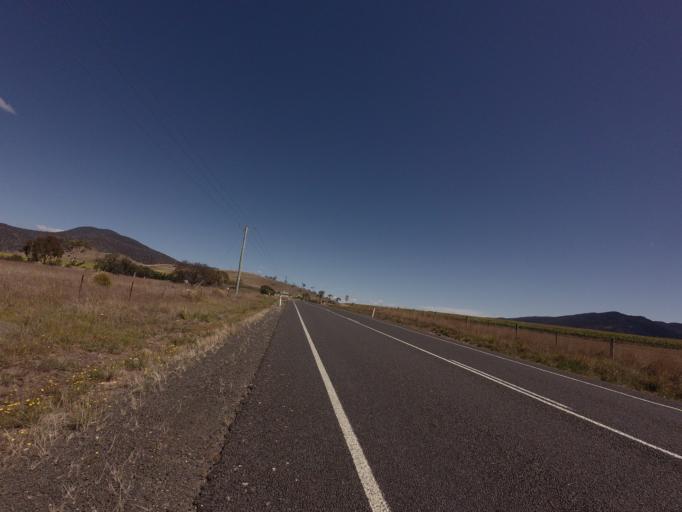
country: AU
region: Tasmania
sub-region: Break O'Day
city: St Helens
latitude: -41.7169
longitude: 147.8348
